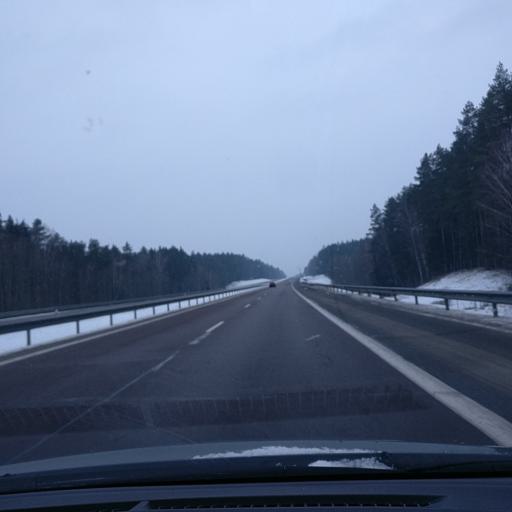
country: LT
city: Sirvintos
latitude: 54.9567
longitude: 24.9586
